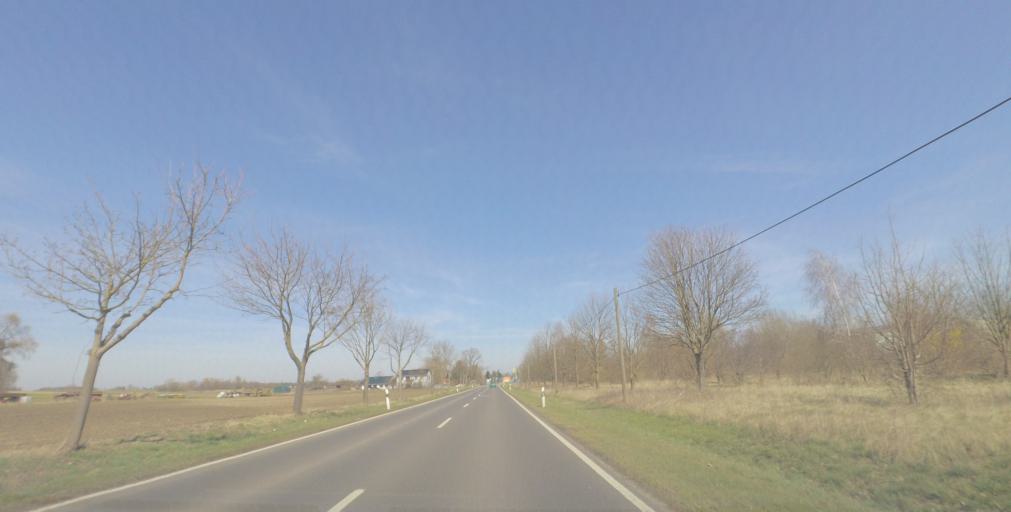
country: DE
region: Brandenburg
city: Neuruppin
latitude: 52.8796
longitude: 12.7907
